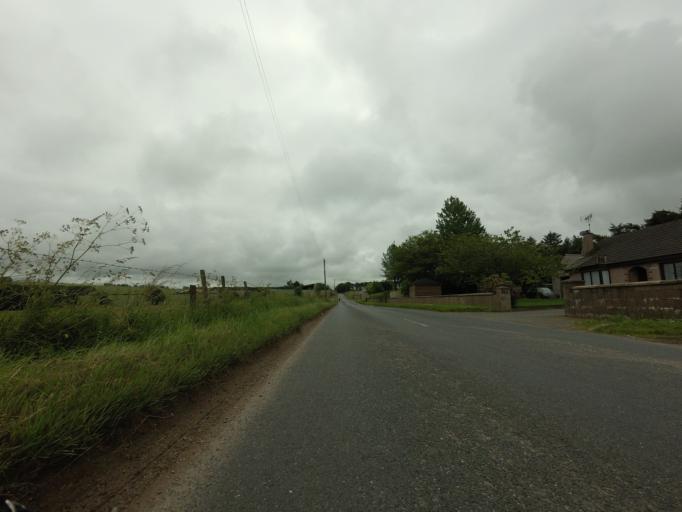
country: GB
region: Scotland
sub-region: Aberdeenshire
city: Turriff
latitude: 57.5428
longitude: -2.3139
